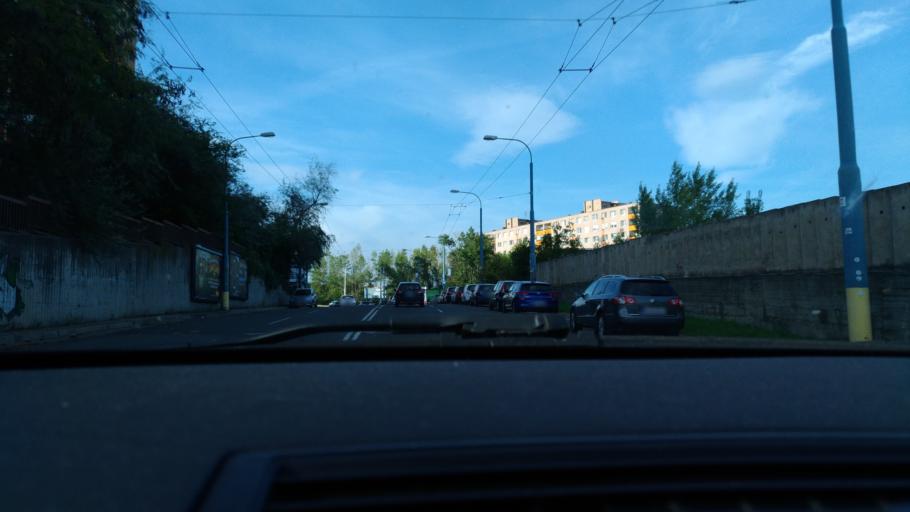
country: SK
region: Bratislavsky
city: Bratislava
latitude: 48.1487
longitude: 17.0562
